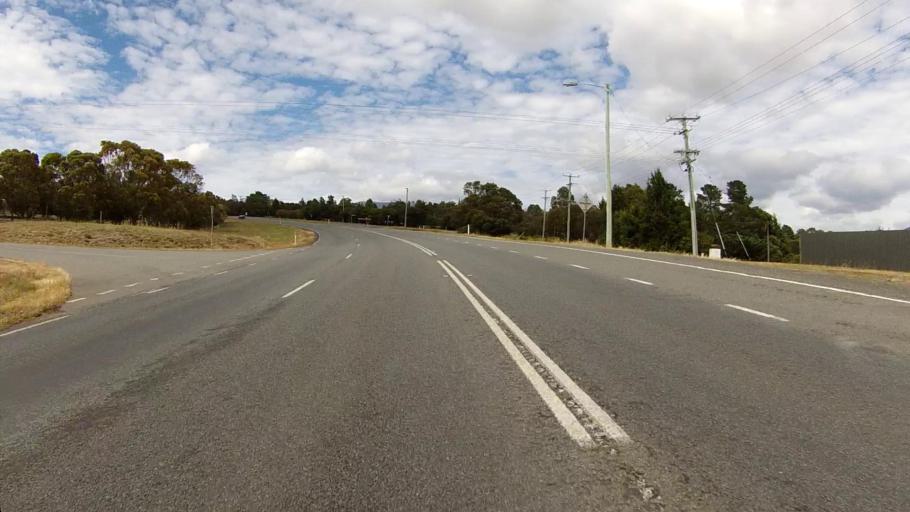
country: AU
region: Tasmania
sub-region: Brighton
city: Old Beach
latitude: -42.7966
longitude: 147.2901
